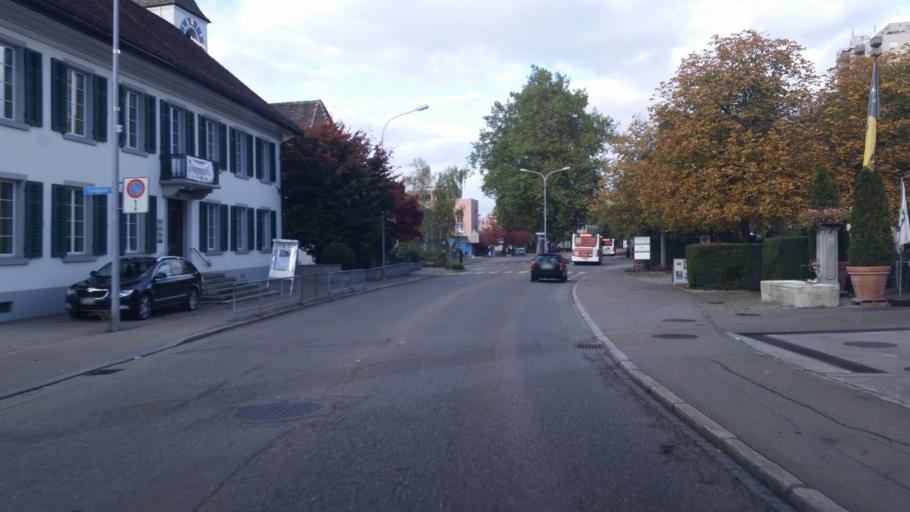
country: CH
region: Zurich
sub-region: Bezirk Dielsdorf
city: Regensdorf / Obstgarten
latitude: 47.4301
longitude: 8.4658
